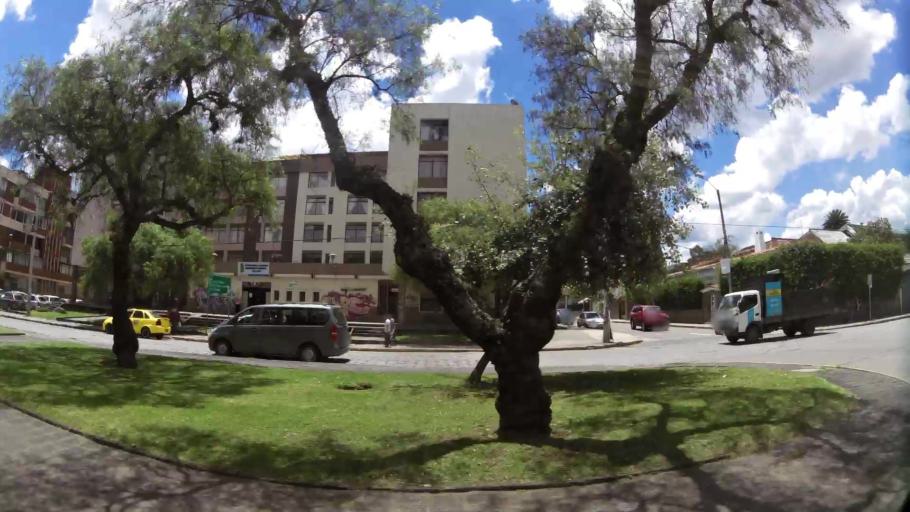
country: EC
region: Azuay
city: Cuenca
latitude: -2.9016
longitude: -79.0072
